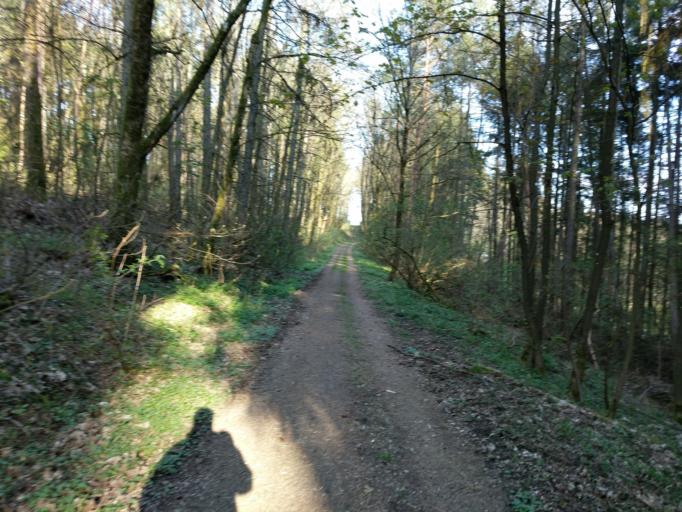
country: DE
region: Hesse
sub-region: Regierungsbezirk Giessen
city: Bad Endbach
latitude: 50.7593
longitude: 8.4857
